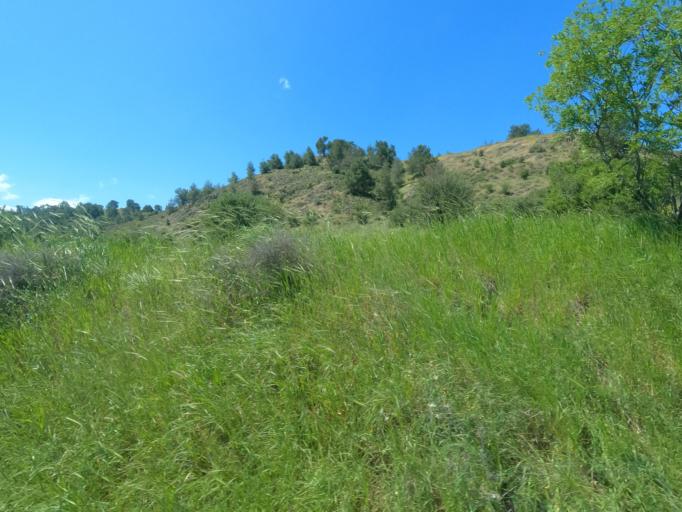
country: CY
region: Lefkosia
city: Peristerona
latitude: 35.0465
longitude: 33.0776
